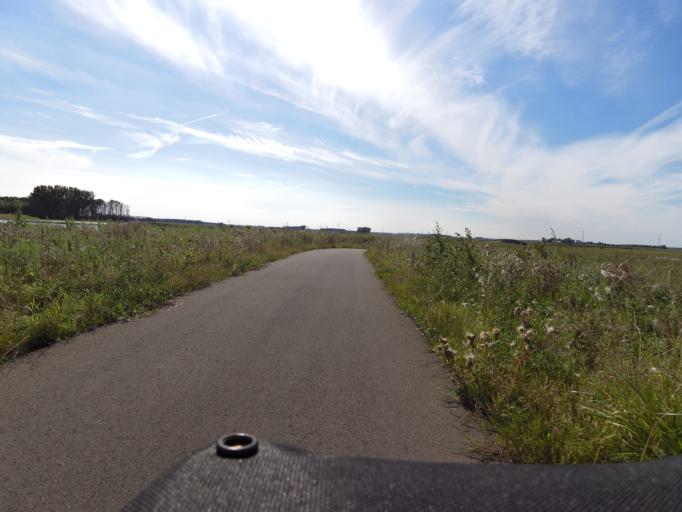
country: NL
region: North Brabant
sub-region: Gemeente Werkendam
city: Werkendam
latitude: 51.7875
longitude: 4.8633
